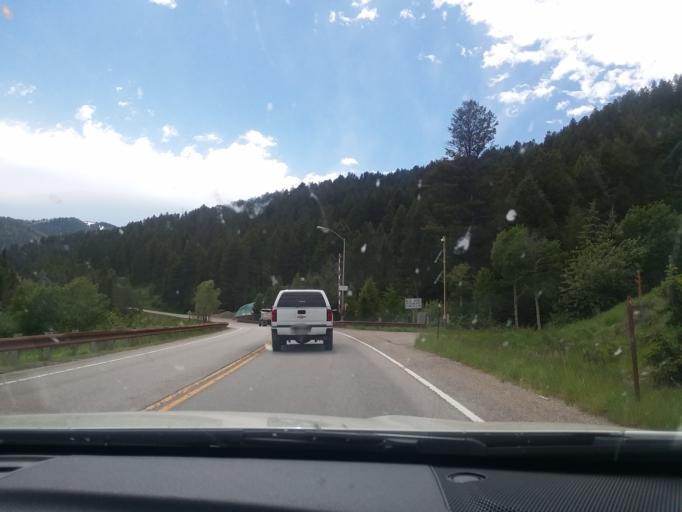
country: US
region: Wyoming
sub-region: Teton County
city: Wilson
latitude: 43.4997
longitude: -110.8994
